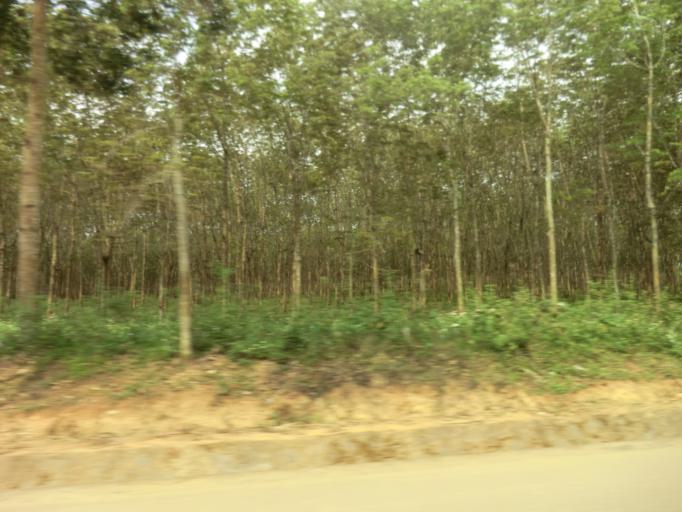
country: VN
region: Thanh Hoa
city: Thi Tran Yen Cat
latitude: 19.4745
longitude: 105.4296
